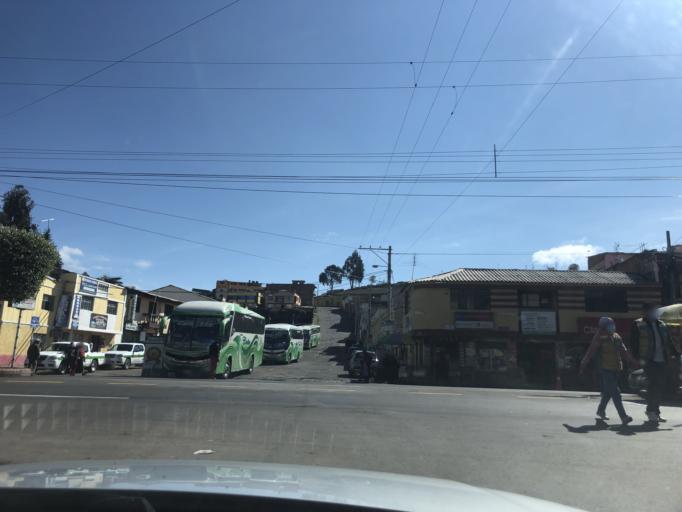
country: EC
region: Chimborazo
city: Riobamba
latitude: -1.7007
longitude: -78.7711
